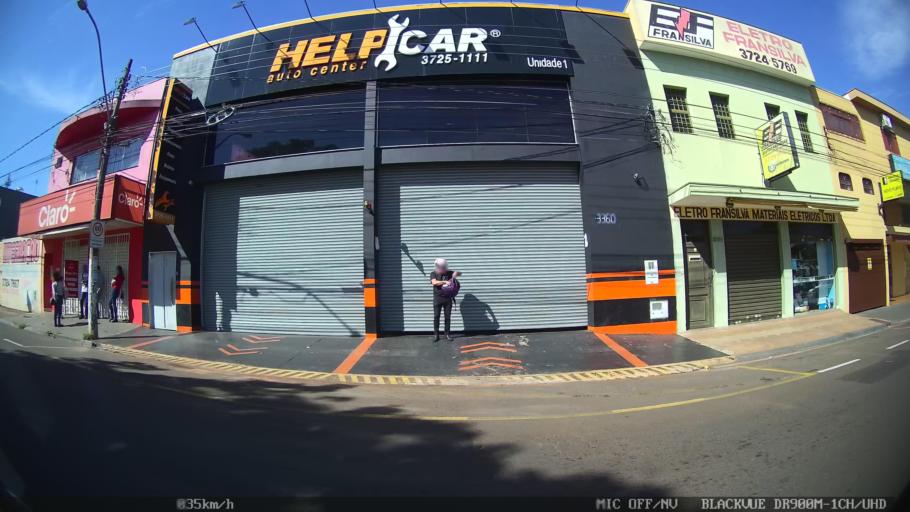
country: BR
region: Sao Paulo
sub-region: Franca
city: Franca
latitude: -20.5216
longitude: -47.4096
